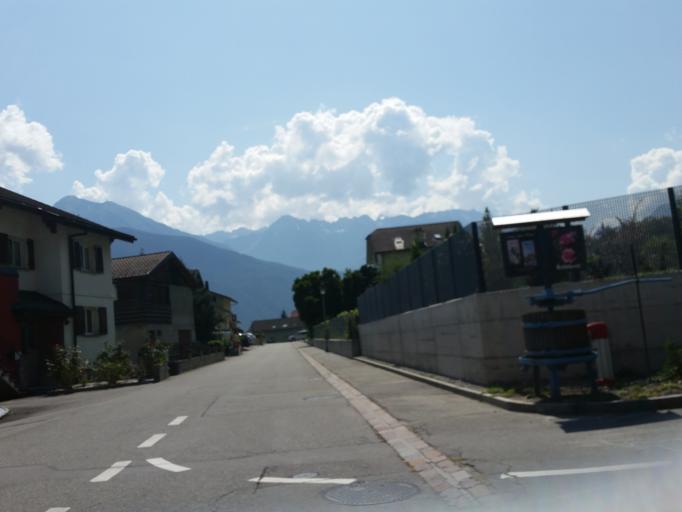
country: CH
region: Valais
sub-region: Martigny District
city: Fully
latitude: 46.1436
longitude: 7.1209
